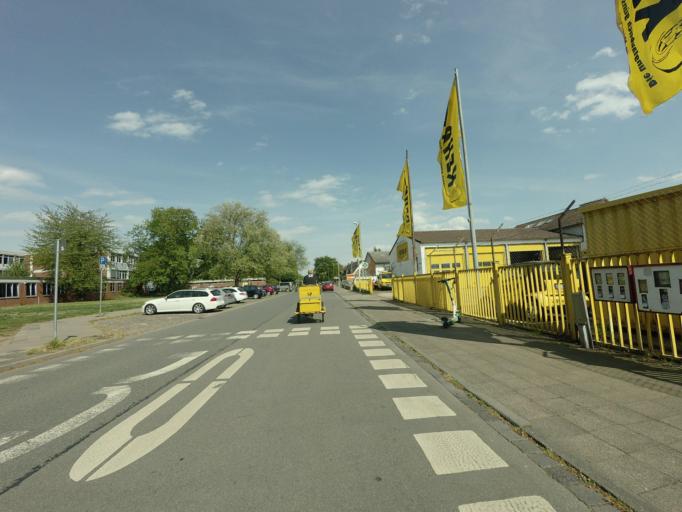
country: DE
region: Lower Saxony
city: Hildesheim
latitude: 52.1622
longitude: 9.9184
